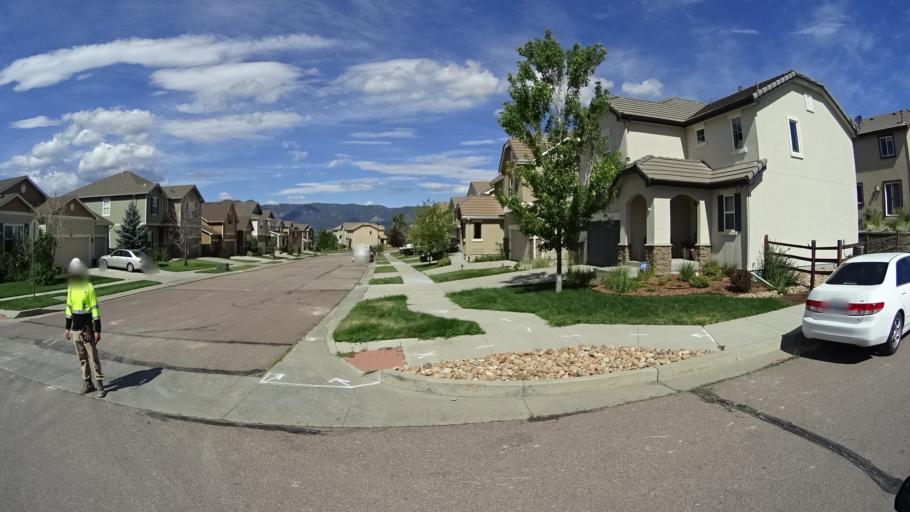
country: US
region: Colorado
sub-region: El Paso County
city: Gleneagle
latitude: 39.0240
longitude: -104.8113
